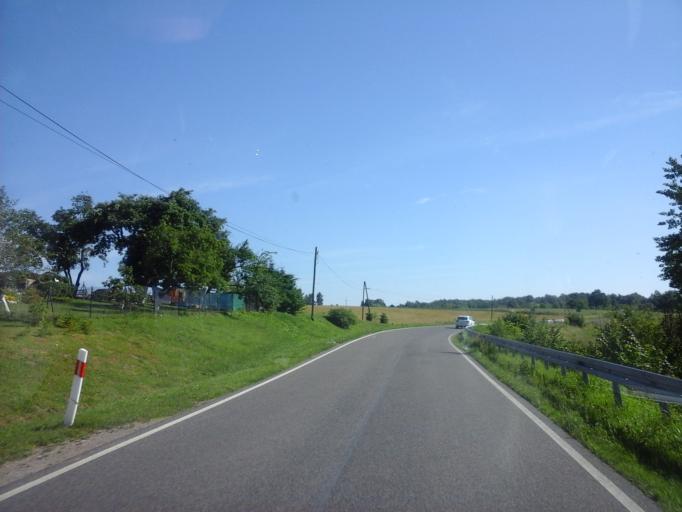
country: PL
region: West Pomeranian Voivodeship
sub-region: Powiat drawski
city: Zlocieniec
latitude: 53.6343
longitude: 15.9410
